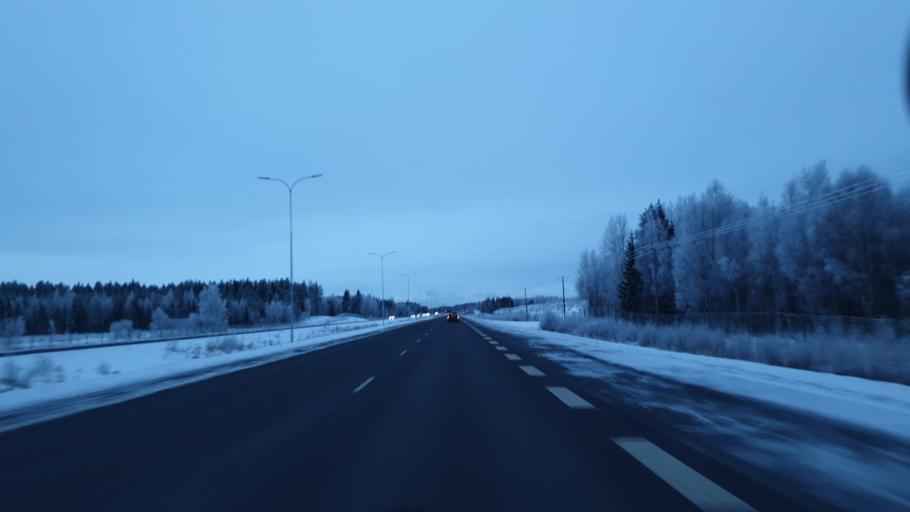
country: FI
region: Northern Ostrobothnia
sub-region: Oulu
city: Haukipudas
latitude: 65.1249
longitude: 25.4309
